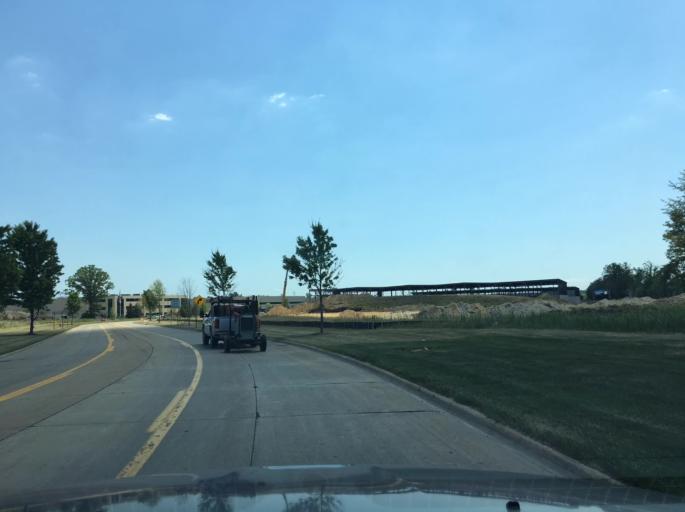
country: US
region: Michigan
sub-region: Macomb County
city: Shelby
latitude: 42.6833
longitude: -83.0146
